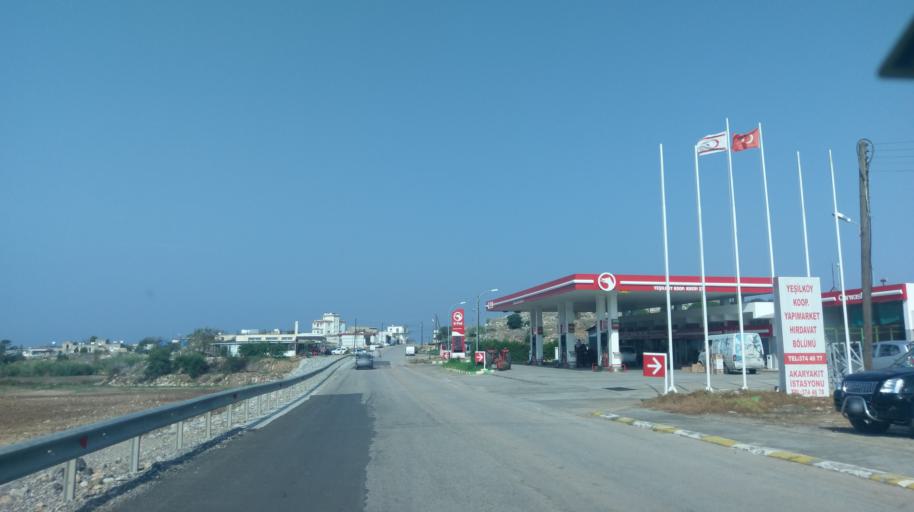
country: CY
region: Ammochostos
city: Leonarisso
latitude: 35.5056
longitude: 34.1612
